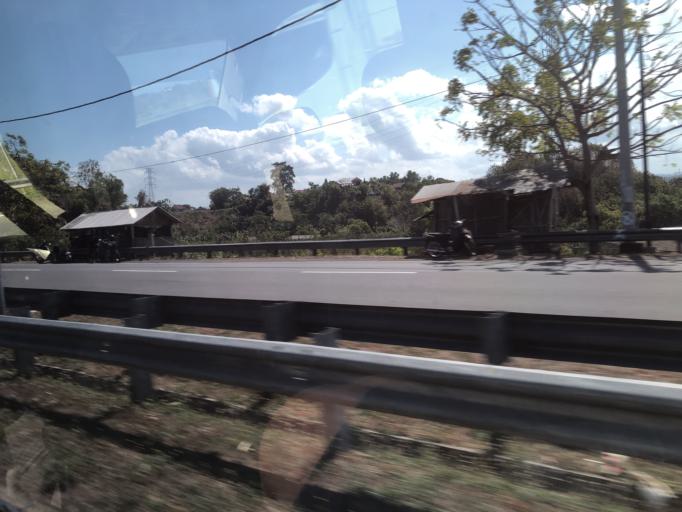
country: ID
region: Bali
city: Dawan
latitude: -8.5584
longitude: 115.4273
